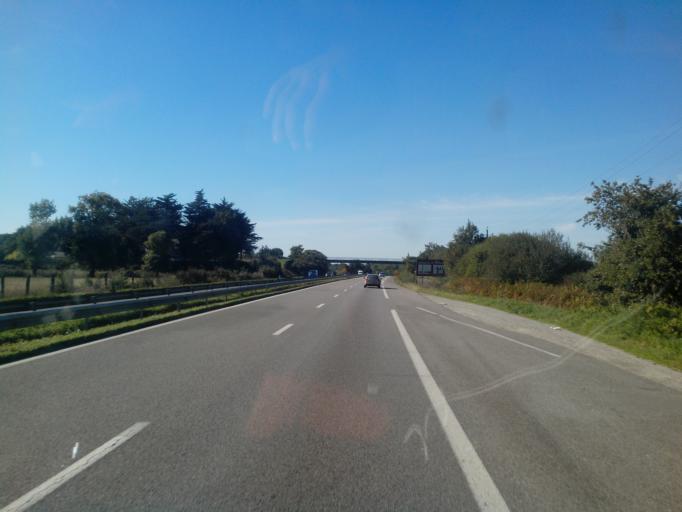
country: FR
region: Brittany
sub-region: Departement du Morbihan
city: Muzillac
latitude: 47.5437
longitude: -2.4326
